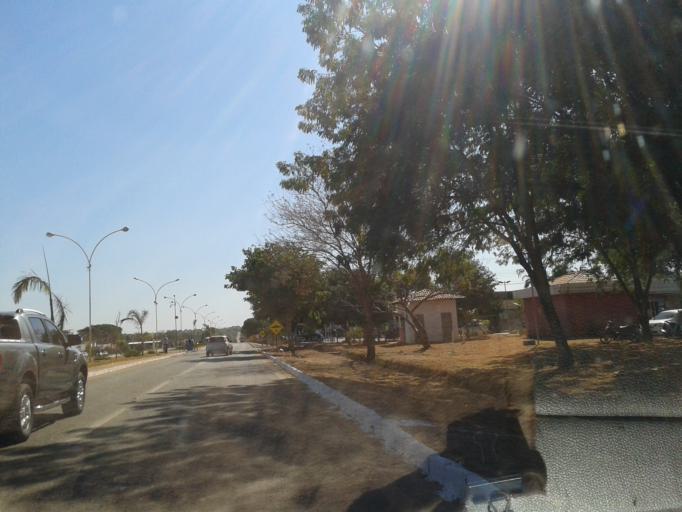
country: BR
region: Goias
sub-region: Crixas
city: Crixas
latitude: -14.0957
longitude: -50.3372
